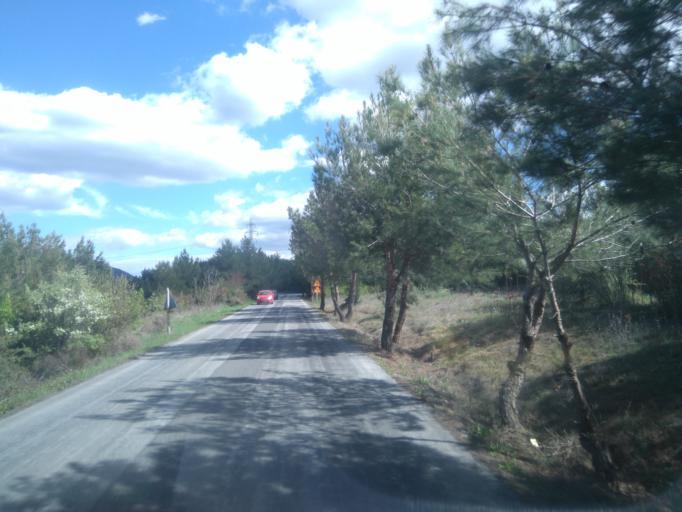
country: GR
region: Central Macedonia
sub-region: Nomos Thessalonikis
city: Asvestochori
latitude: 40.6416
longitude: 23.0057
